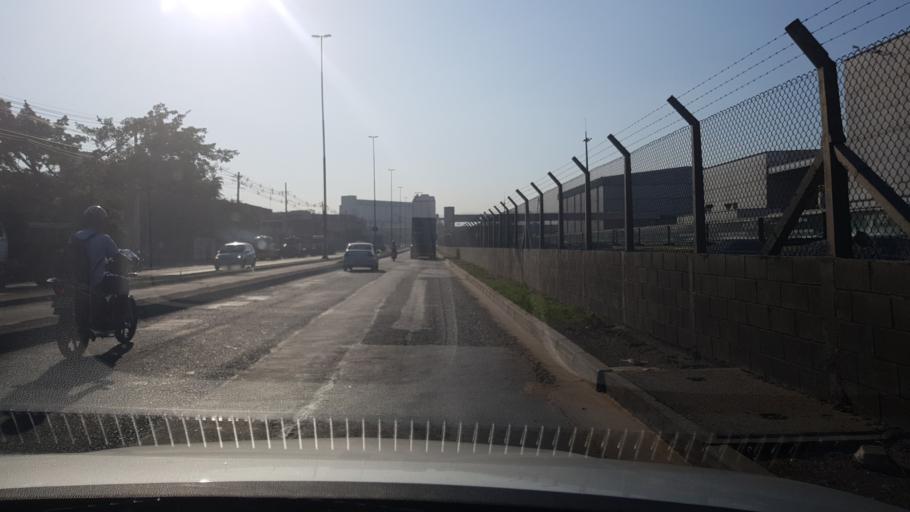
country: BR
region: Sao Paulo
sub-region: Santos
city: Santos
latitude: -23.9646
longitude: -46.3033
